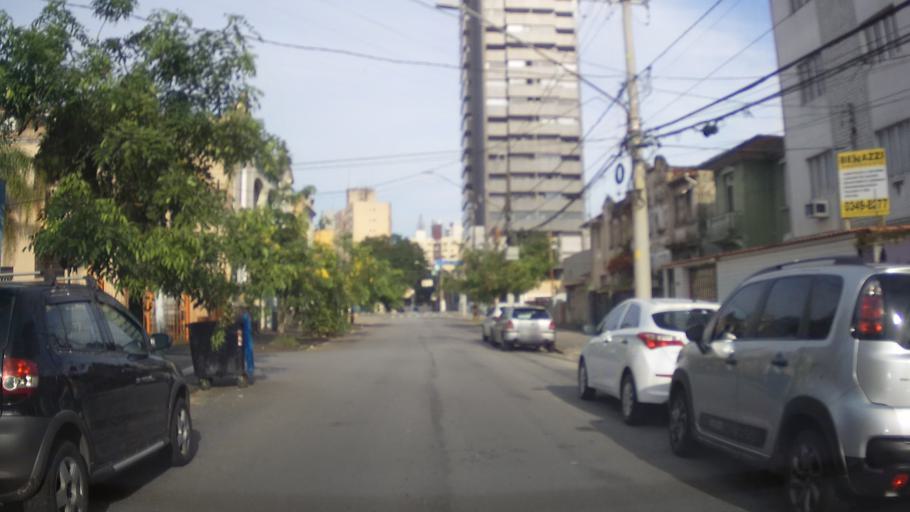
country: BR
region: Sao Paulo
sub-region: Santos
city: Santos
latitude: -23.9529
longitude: -46.3214
